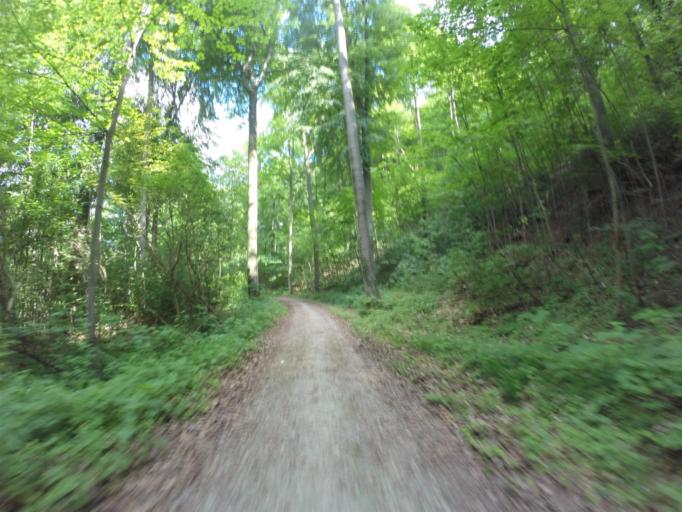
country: DE
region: Thuringia
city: Jena
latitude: 50.9247
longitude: 11.6298
